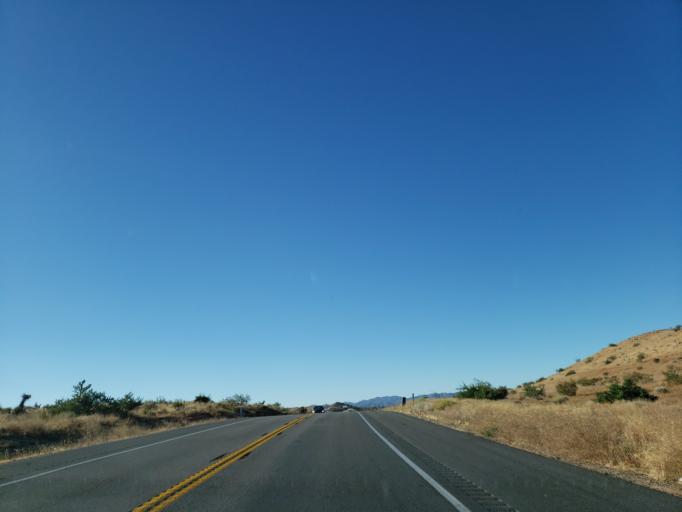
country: US
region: California
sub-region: San Bernardino County
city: Yucca Valley
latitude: 34.1852
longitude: -116.4312
